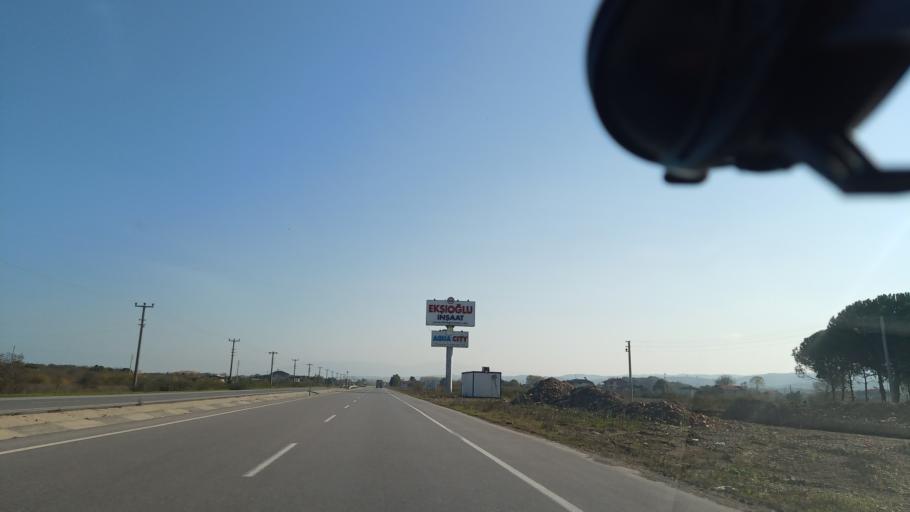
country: TR
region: Sakarya
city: Karasu
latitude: 41.0848
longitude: 30.7559
